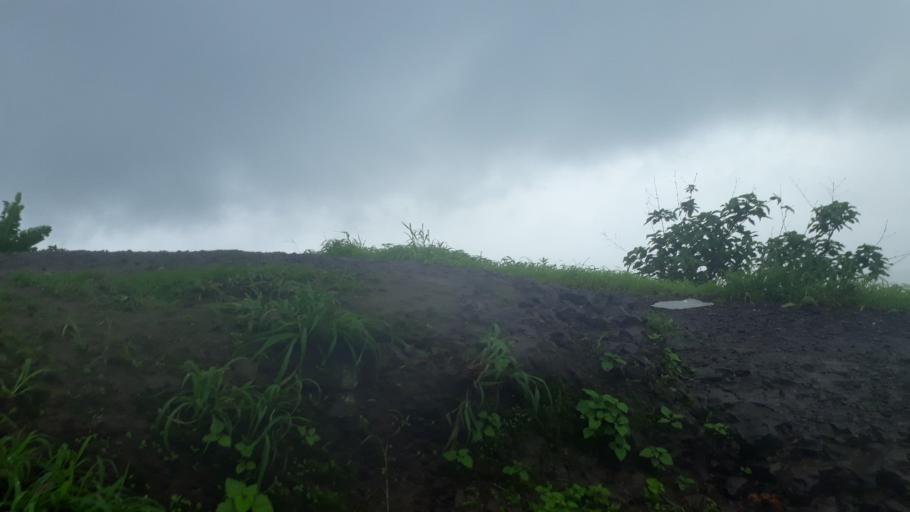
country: IN
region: Maharashtra
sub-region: Pune Division
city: Wadgaon
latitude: 18.6314
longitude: 73.5171
